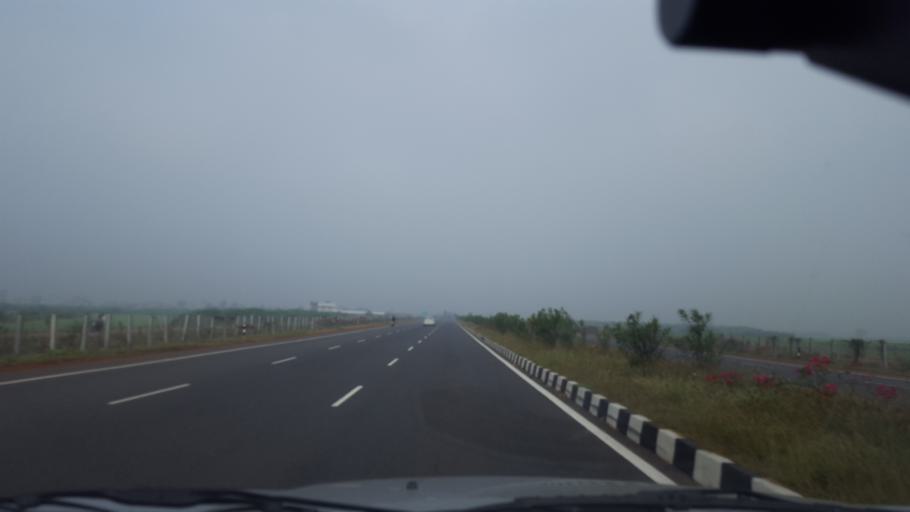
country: IN
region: Andhra Pradesh
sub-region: Prakasam
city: Ongole
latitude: 15.5243
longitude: 80.0614
